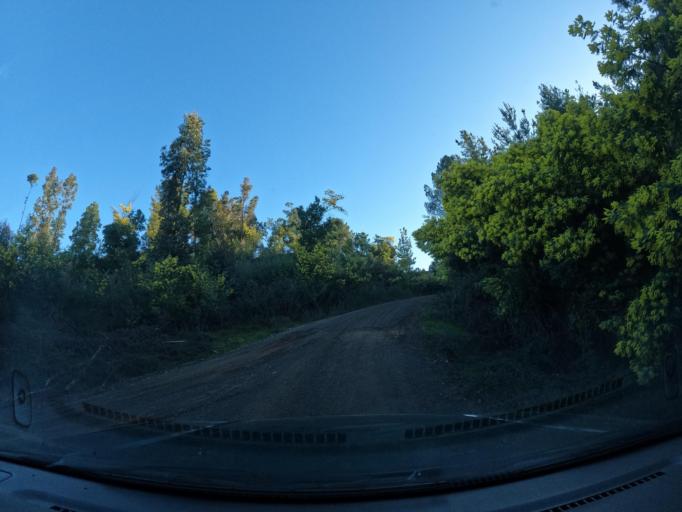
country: CL
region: Biobio
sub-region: Provincia de Concepcion
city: Chiguayante
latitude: -37.0162
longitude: -72.8394
